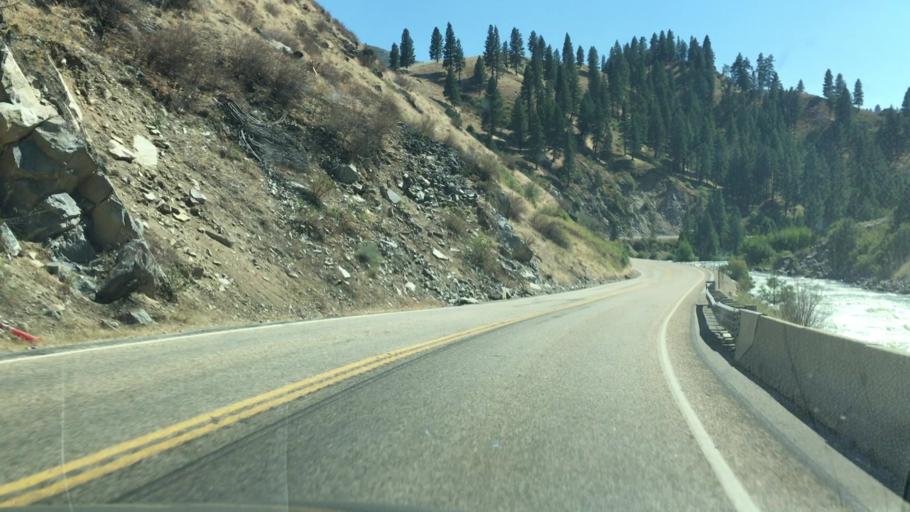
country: US
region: Idaho
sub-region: Boise County
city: Idaho City
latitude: 44.1028
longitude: -116.0946
